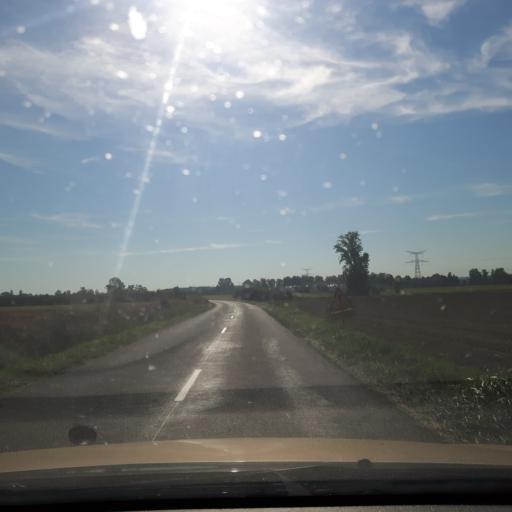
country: FR
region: Midi-Pyrenees
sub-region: Departement de la Haute-Garonne
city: Villeneuve-les-Bouloc
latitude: 43.7594
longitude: 1.4269
